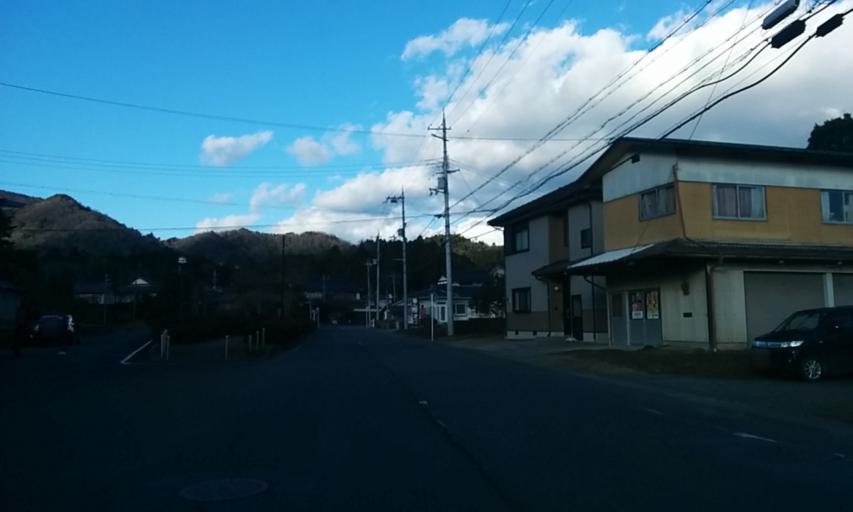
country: JP
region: Kyoto
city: Fukuchiyama
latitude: 35.3102
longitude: 135.1557
